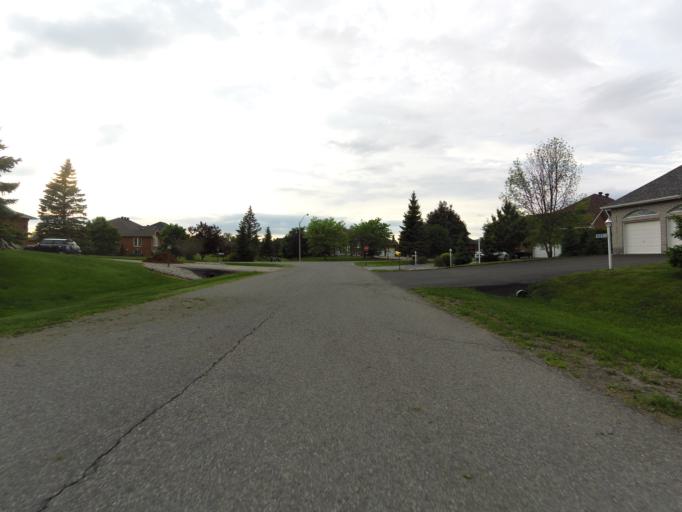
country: CA
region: Ontario
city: Ottawa
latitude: 45.2696
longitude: -75.5779
